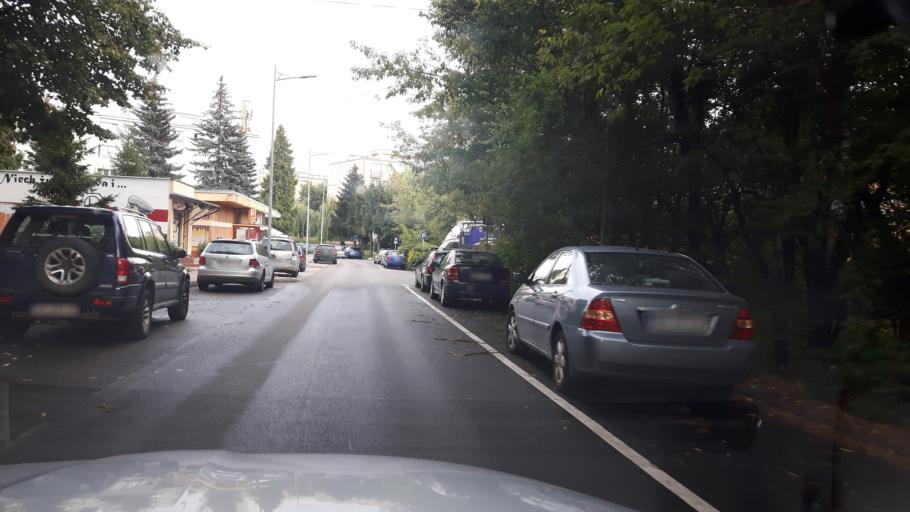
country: PL
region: Masovian Voivodeship
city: Zielonka
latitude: 52.3152
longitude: 21.1587
